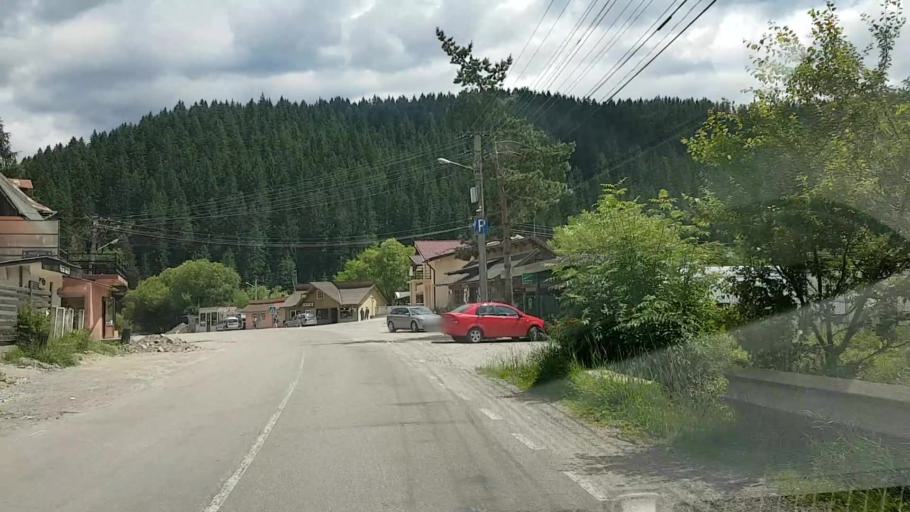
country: RO
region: Suceava
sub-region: Comuna Brosteni
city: Brosteni
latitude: 47.2377
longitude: 25.6948
